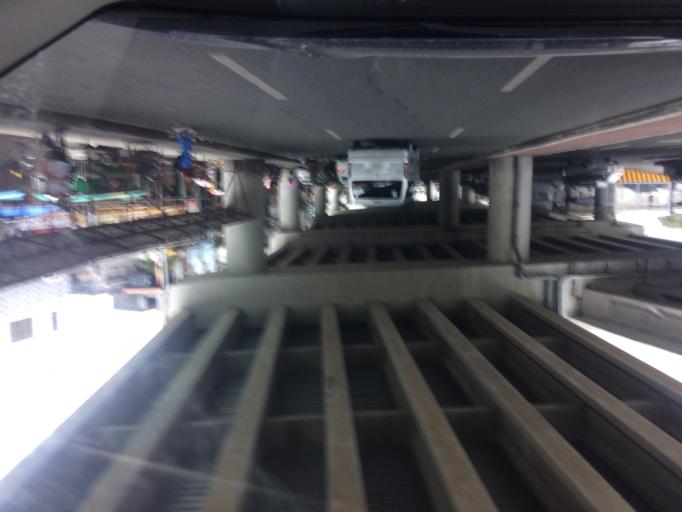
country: PH
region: Metro Manila
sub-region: Makati City
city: Makati City
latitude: 14.5254
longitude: 121.0116
